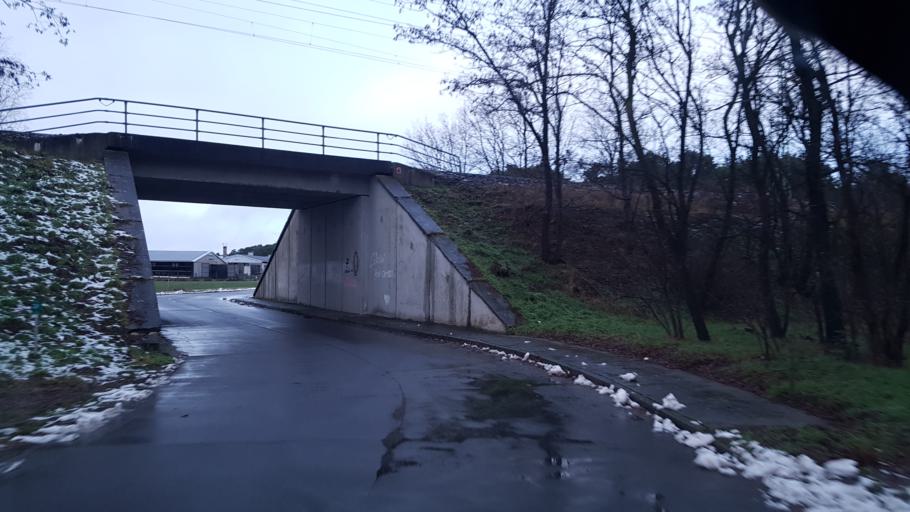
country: DE
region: Brandenburg
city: Janschwalde
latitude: 51.8684
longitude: 14.5091
